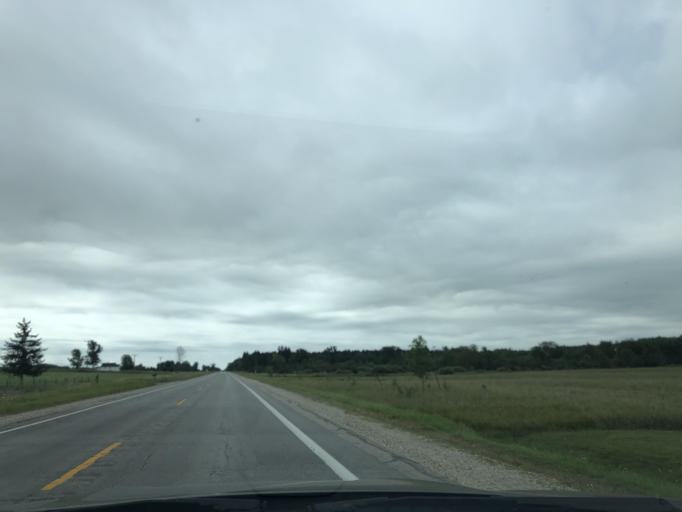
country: US
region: Michigan
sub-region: Missaukee County
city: Lake City
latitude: 44.2174
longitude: -85.2146
